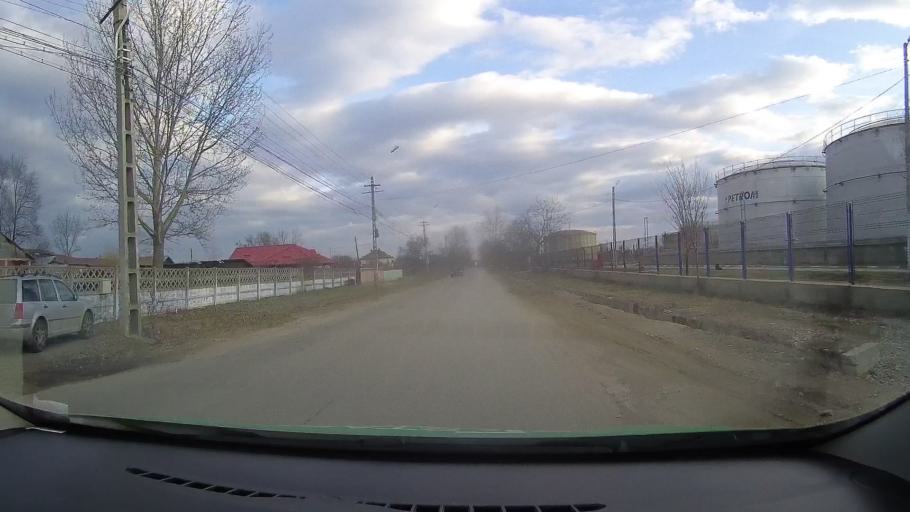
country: RO
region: Dambovita
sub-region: Municipiul Moreni
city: Moreni
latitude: 44.9663
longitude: 25.6541
